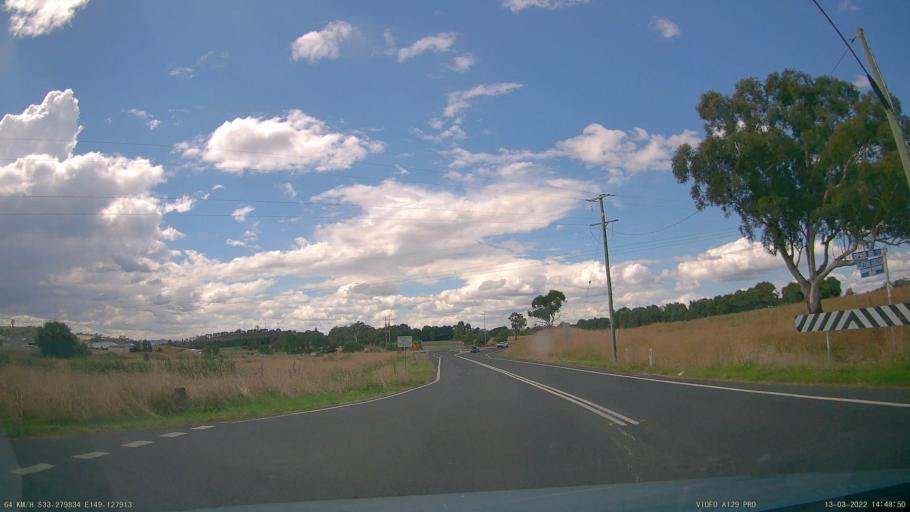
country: AU
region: New South Wales
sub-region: Orange Municipality
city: Orange
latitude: -33.2797
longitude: 149.1281
